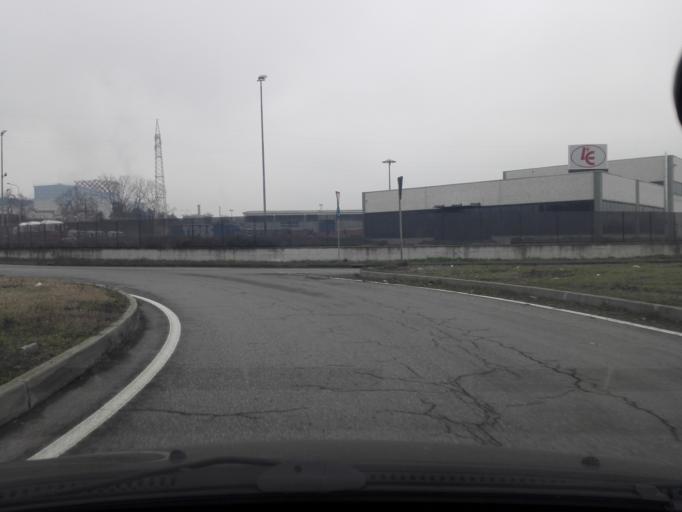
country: IT
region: Piedmont
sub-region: Provincia di Alessandria
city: Pasturana
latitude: 44.7797
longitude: 8.7549
